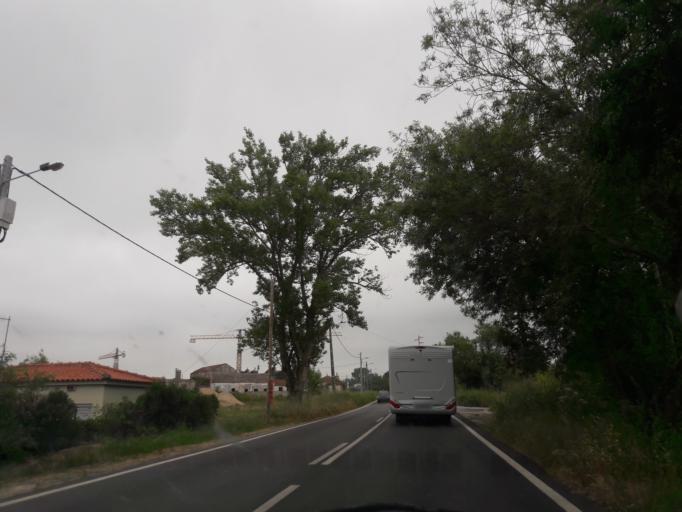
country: PT
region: Leiria
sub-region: Obidos
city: Obidos
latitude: 39.3674
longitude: -9.1464
